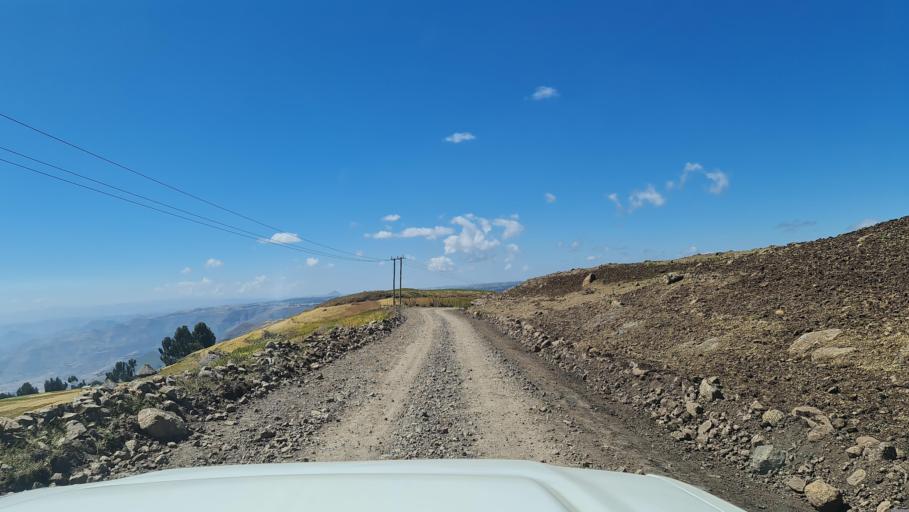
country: ET
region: Amhara
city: Debark'
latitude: 13.2299
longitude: 38.0986
